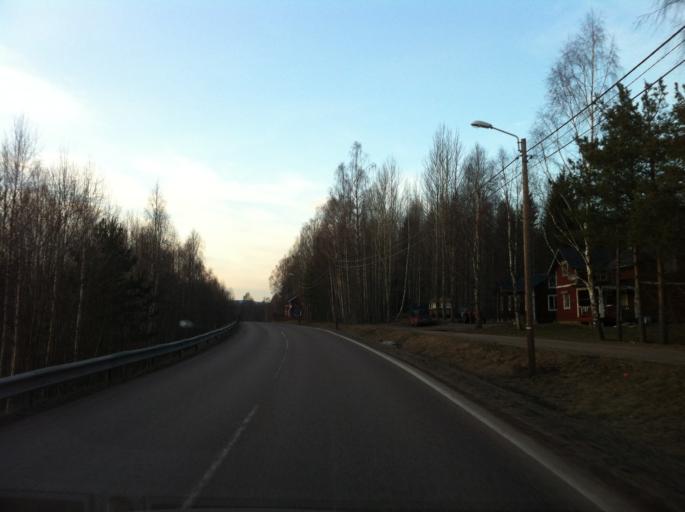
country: SE
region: Dalarna
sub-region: Vansbro Kommun
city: Vansbro
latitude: 60.5238
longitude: 14.2198
